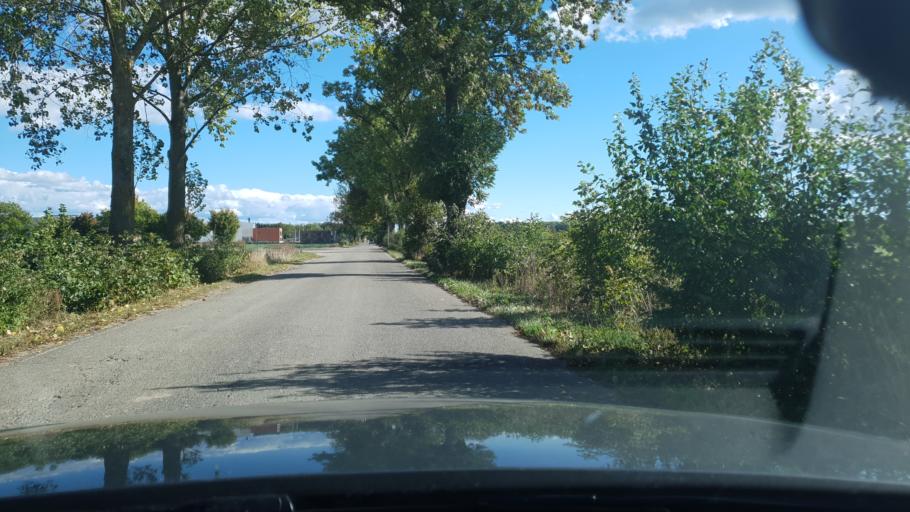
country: PL
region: Pomeranian Voivodeship
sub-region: Powiat pucki
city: Zelistrzewo
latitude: 54.6871
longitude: 18.4470
